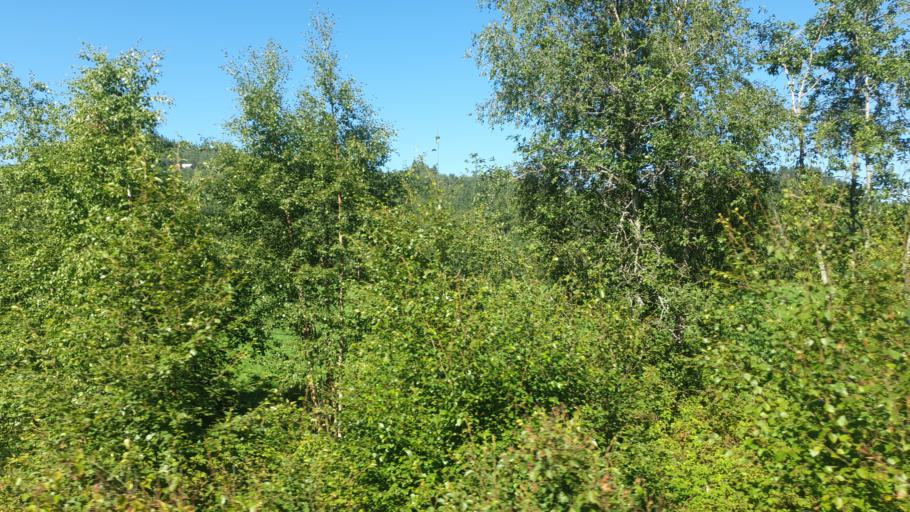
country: NO
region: Sor-Trondelag
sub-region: Meldal
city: Meldal
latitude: 63.1804
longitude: 9.7650
